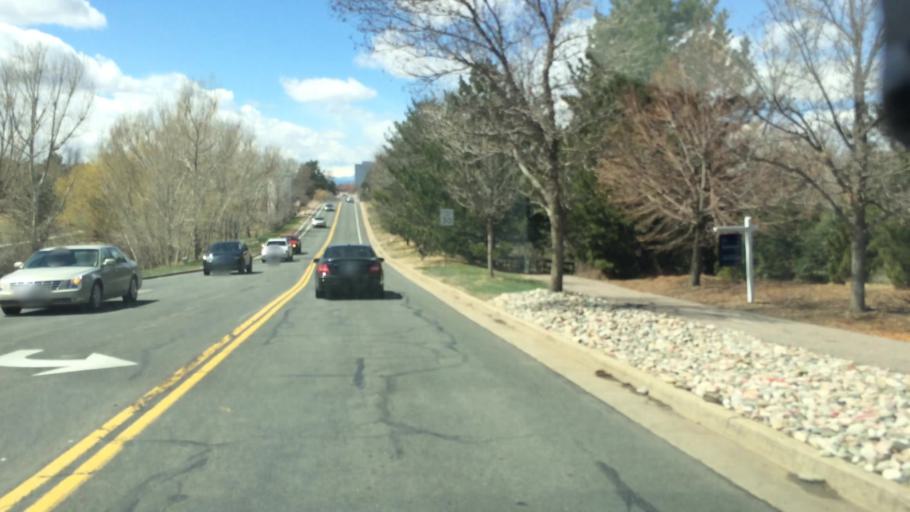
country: US
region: Colorado
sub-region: Arapahoe County
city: Centennial
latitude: 39.6096
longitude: -104.8764
